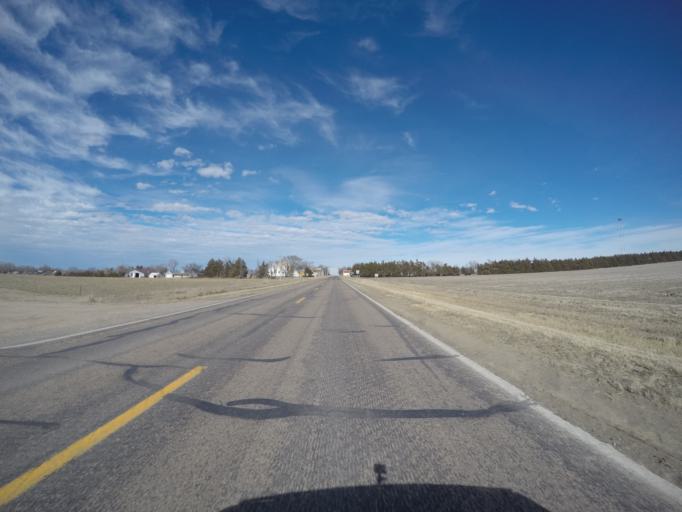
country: US
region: Nebraska
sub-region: Franklin County
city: Franklin
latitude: 40.2017
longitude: -98.9525
